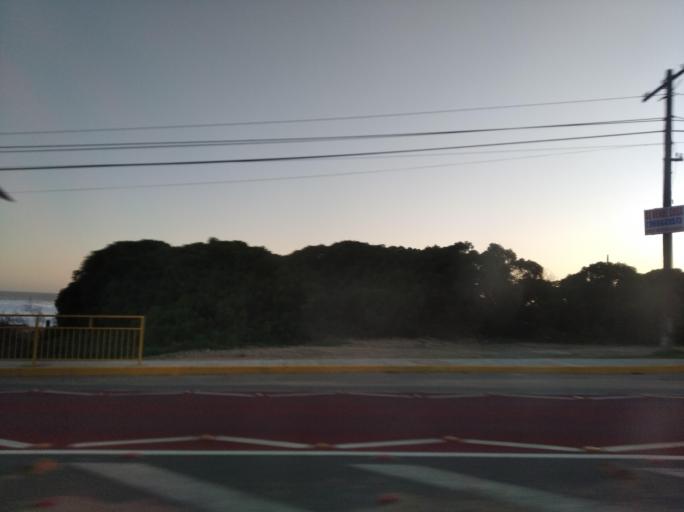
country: CL
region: Valparaiso
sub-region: San Antonio Province
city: El Tabo
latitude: -33.4494
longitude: -71.6758
